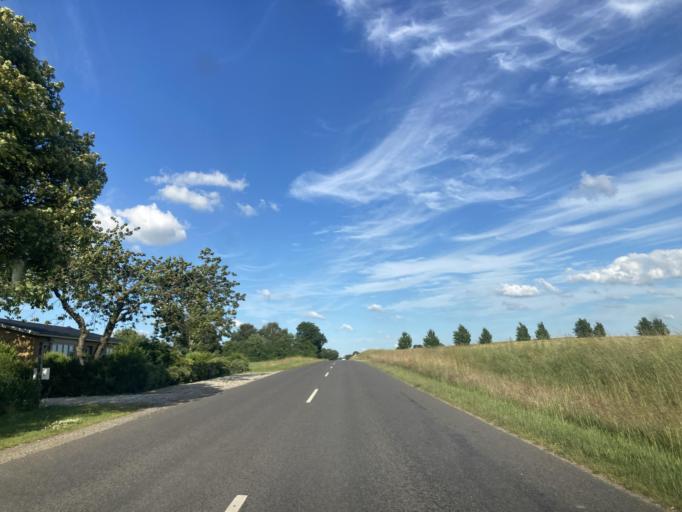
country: DK
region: South Denmark
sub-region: Kolding Kommune
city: Lunderskov
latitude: 55.4858
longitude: 9.3409
